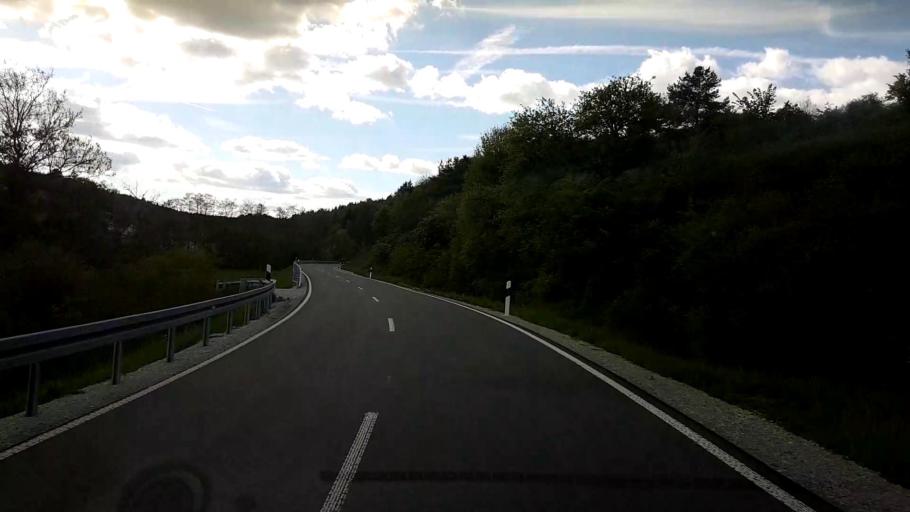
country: DE
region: Bavaria
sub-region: Upper Franconia
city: Hollfeld
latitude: 49.9520
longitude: 11.2762
